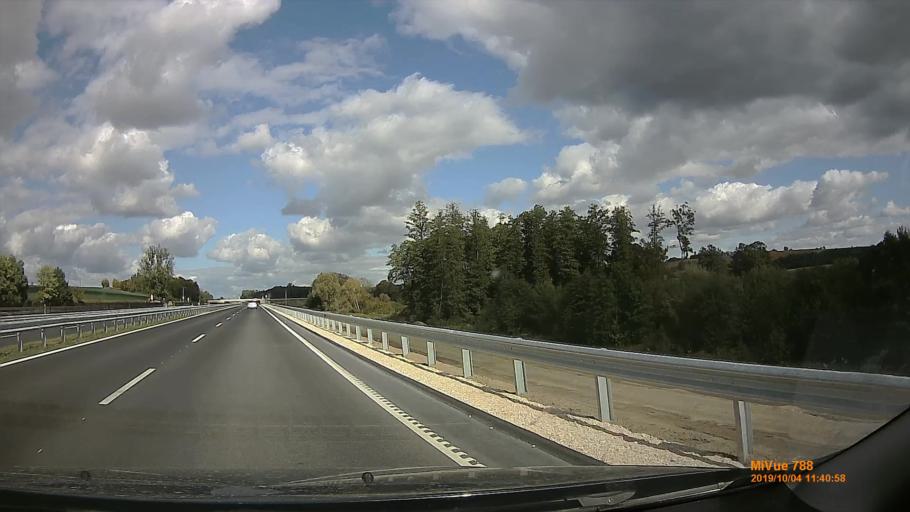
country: HU
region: Somogy
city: Karad
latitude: 46.5716
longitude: 17.8067
